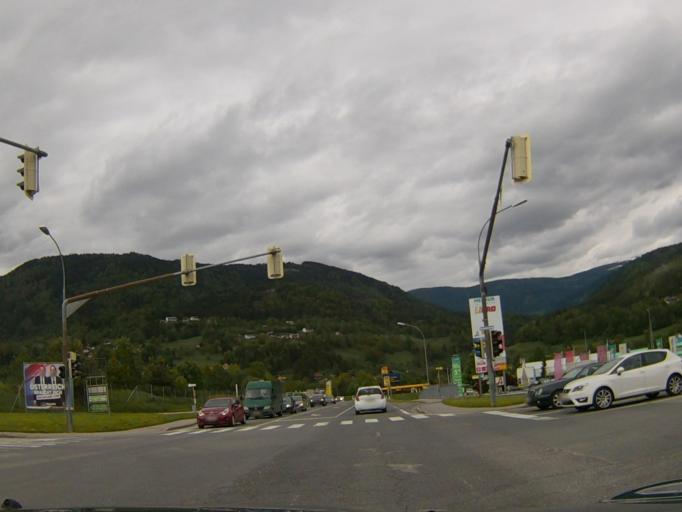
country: AT
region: Carinthia
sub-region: Villach Stadt
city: Villach
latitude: 46.6293
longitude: 13.8233
